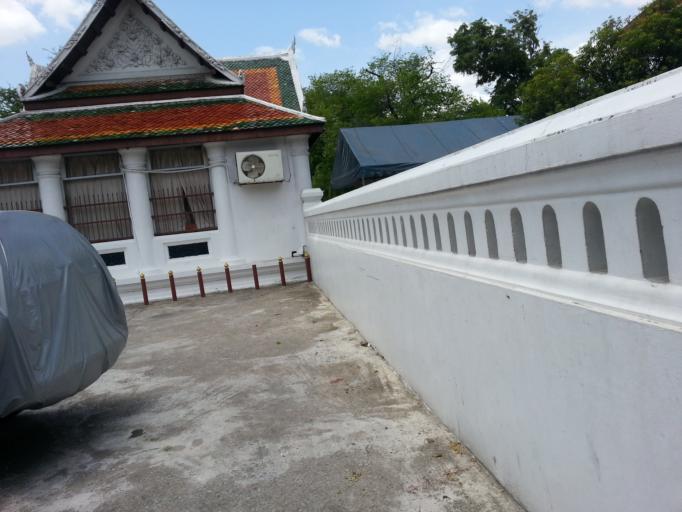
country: TH
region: Bangkok
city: Pom Prap Sattru Phai
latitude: 13.7612
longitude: 100.5108
